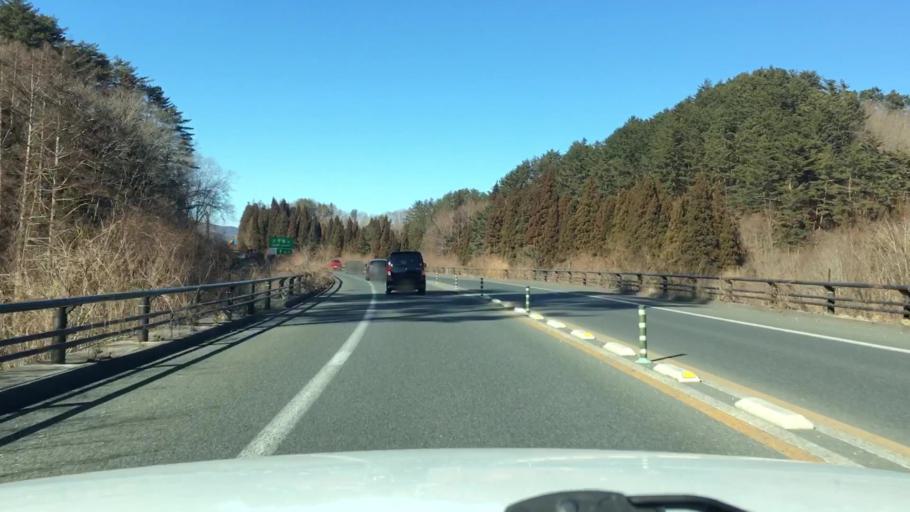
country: JP
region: Iwate
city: Miyako
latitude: 39.6154
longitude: 141.9344
